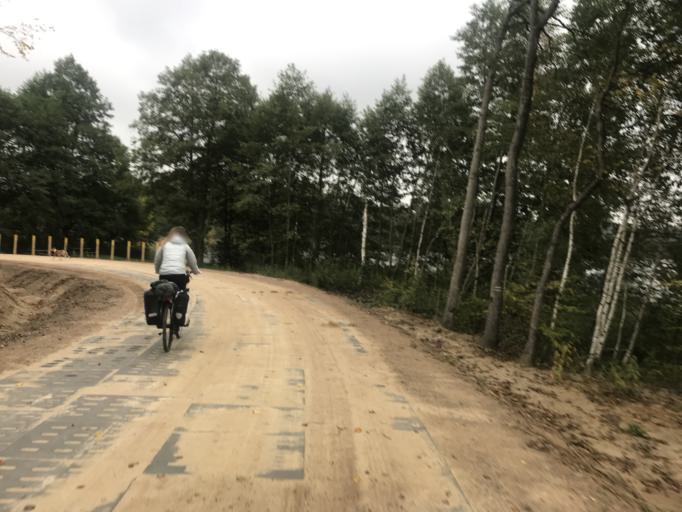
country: PL
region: West Pomeranian Voivodeship
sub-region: Powiat walecki
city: Miroslawiec
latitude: 53.3506
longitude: 16.0097
